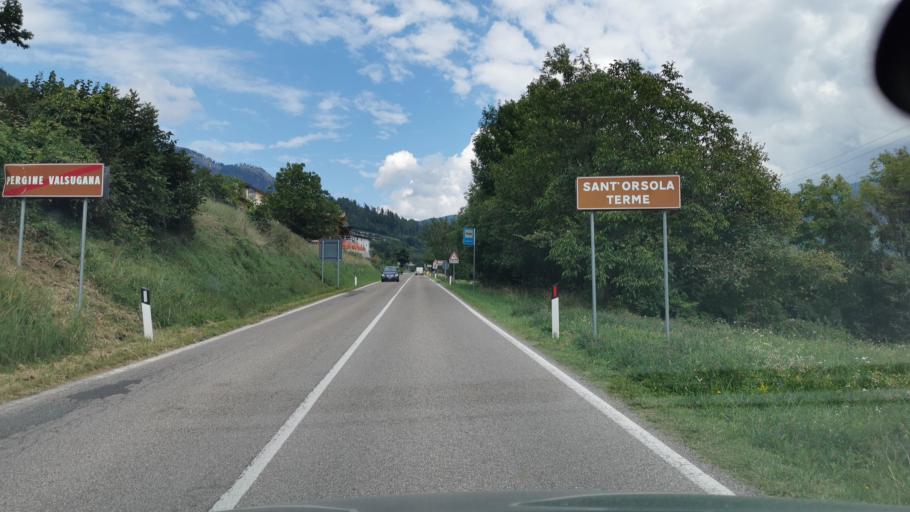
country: IT
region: Trentino-Alto Adige
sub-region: Provincia di Trento
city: Frassilongo
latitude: 46.0865
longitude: 11.2780
